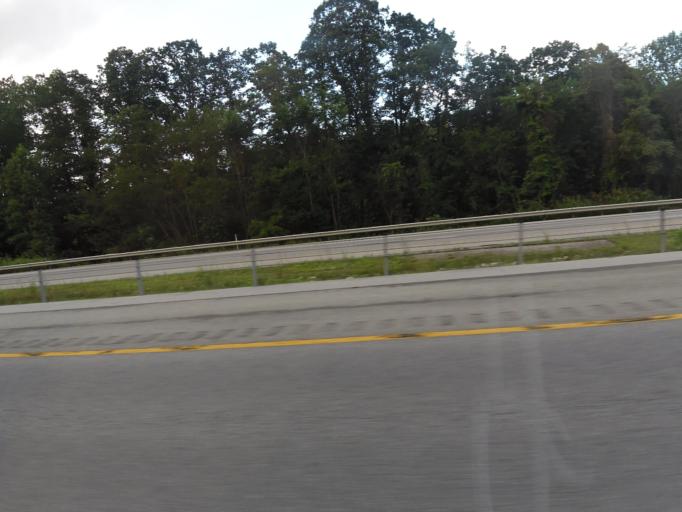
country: US
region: Kentucky
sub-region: Rockcastle County
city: Mount Vernon
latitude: 37.3002
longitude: -84.2789
